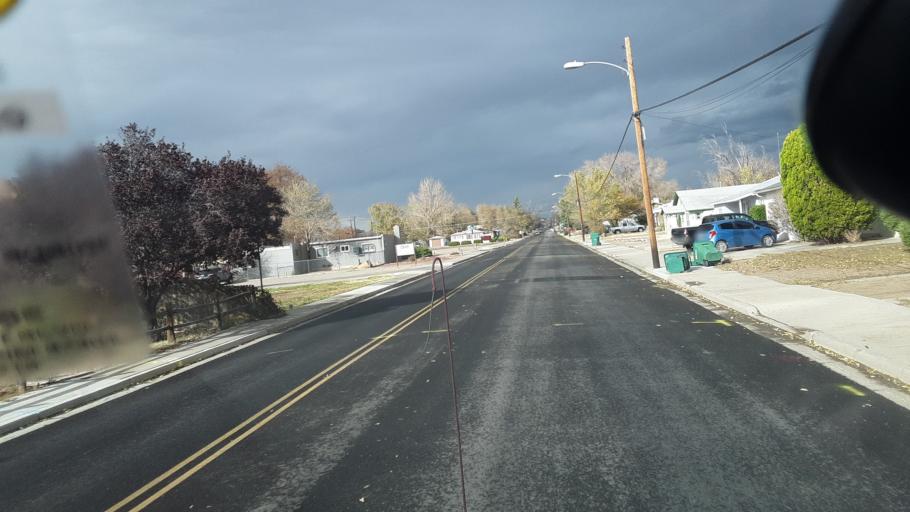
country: US
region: New Mexico
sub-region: San Juan County
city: Farmington
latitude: 36.7366
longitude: -108.1979
